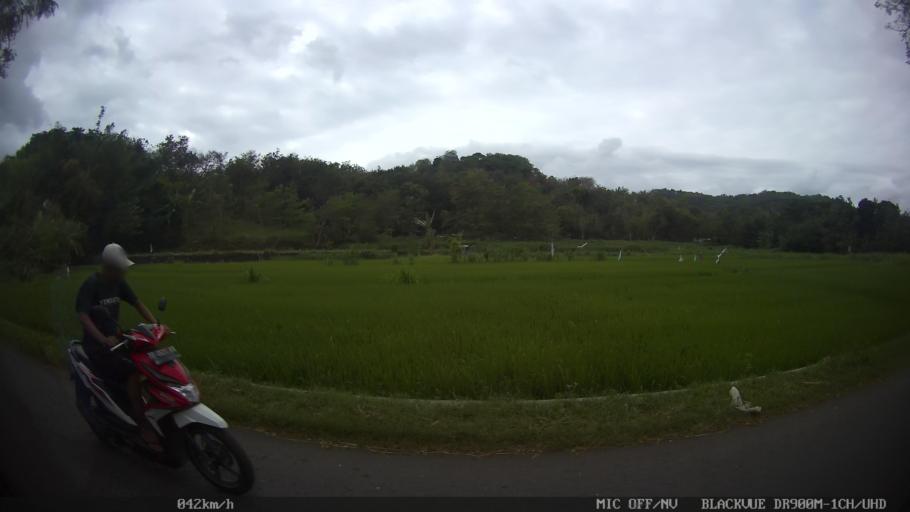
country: ID
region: Daerah Istimewa Yogyakarta
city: Sewon
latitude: -7.8668
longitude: 110.4200
